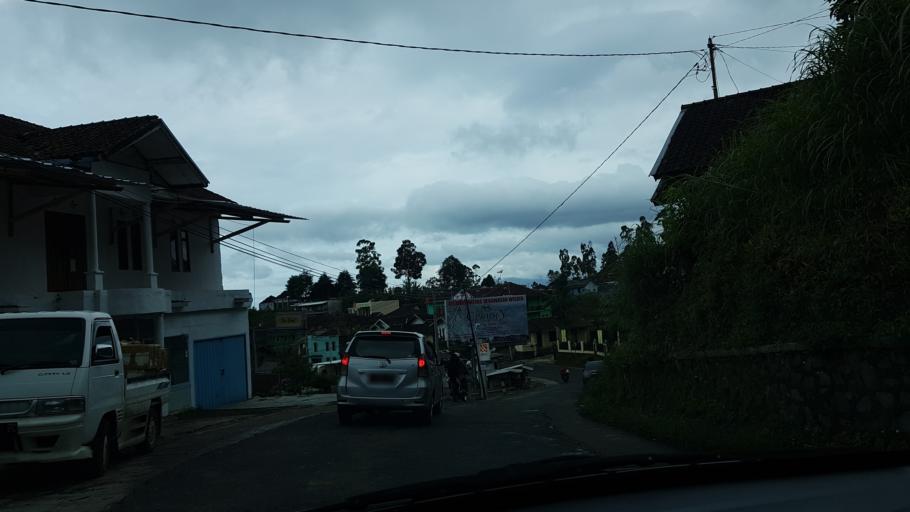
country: ID
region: West Java
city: Banjar
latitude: -7.1352
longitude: 107.4159
